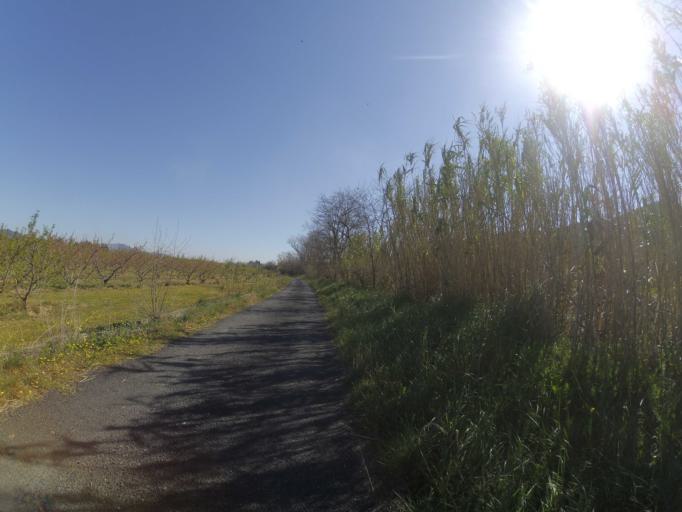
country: FR
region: Languedoc-Roussillon
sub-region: Departement des Pyrenees-Orientales
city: Ille-sur-Tet
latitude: 42.6545
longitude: 2.6048
